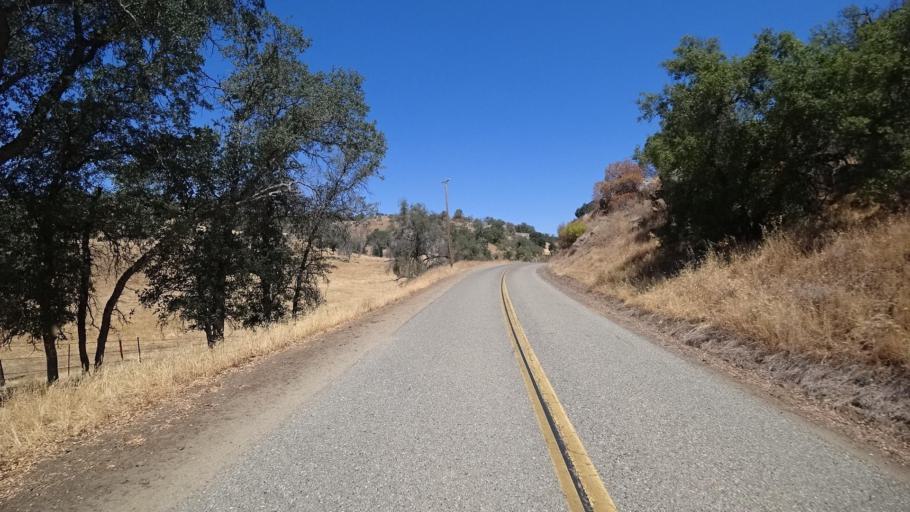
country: US
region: California
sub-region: Mariposa County
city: Mariposa
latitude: 37.2883
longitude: -119.9770
